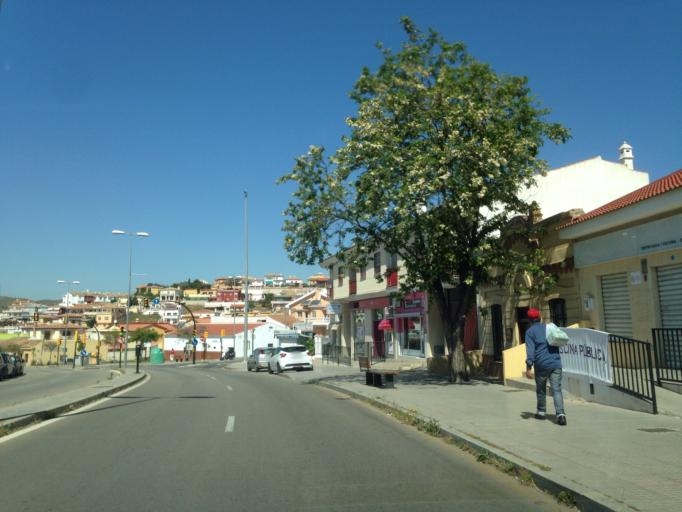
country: ES
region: Andalusia
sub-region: Provincia de Malaga
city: Malaga
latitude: 36.7399
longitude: -4.4820
